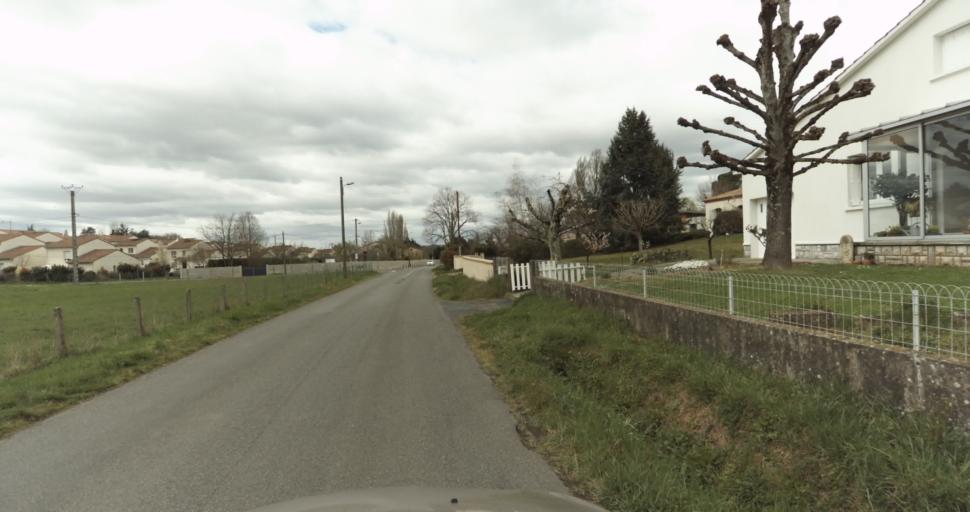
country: FR
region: Midi-Pyrenees
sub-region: Departement du Tarn
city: Puygouzon
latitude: 43.9116
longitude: 2.1691
